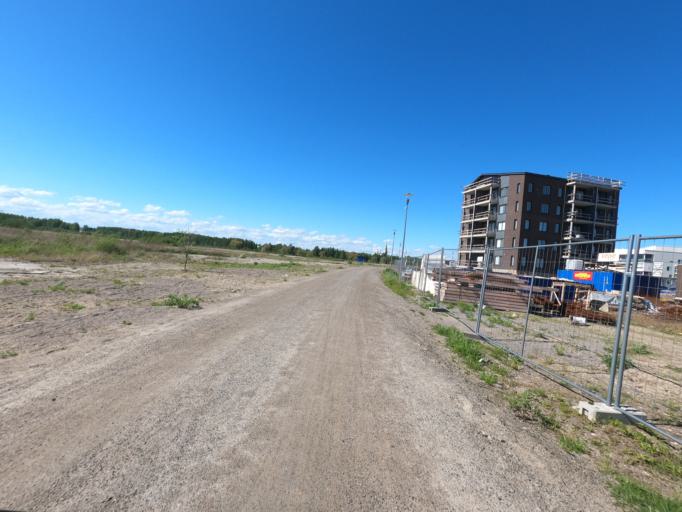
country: FI
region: North Karelia
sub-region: Joensuu
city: Joensuu
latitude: 62.5887
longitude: 29.7603
